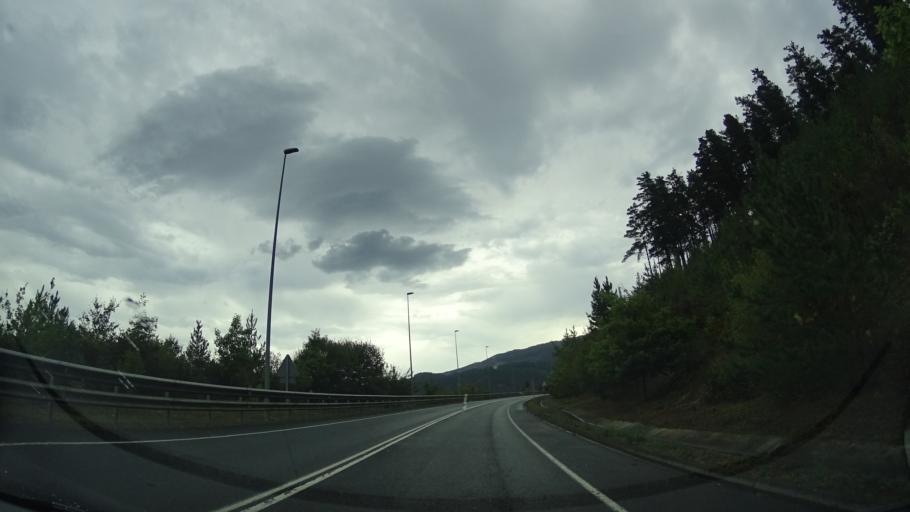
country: ES
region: Basque Country
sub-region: Bizkaia
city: Areatza
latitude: 43.1571
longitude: -2.7864
